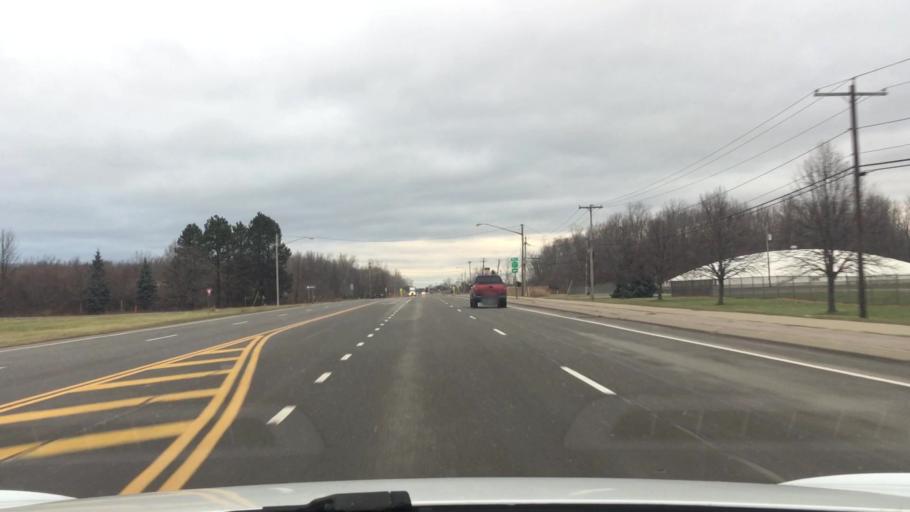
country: US
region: New York
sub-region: Erie County
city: Grandyle Village
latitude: 43.0737
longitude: -78.9405
